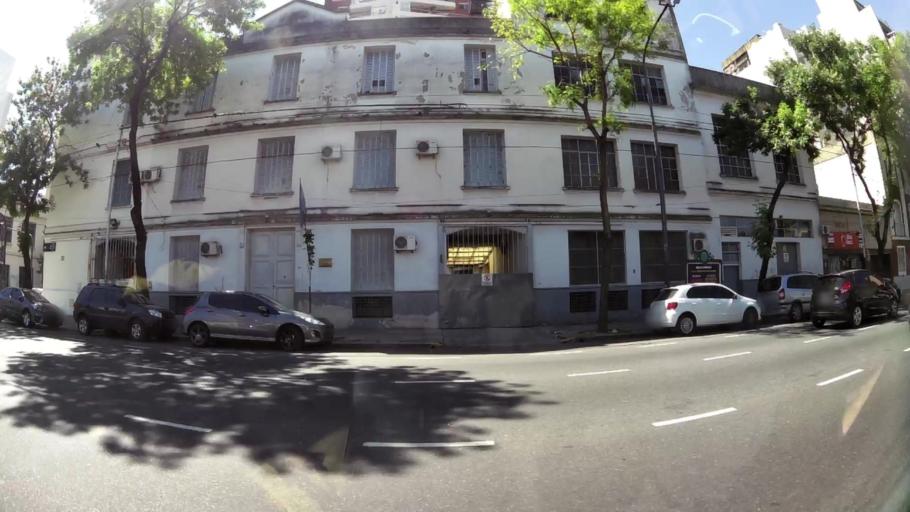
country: AR
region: Buenos Aires F.D.
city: Villa Santa Rita
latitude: -34.6310
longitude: -58.4529
